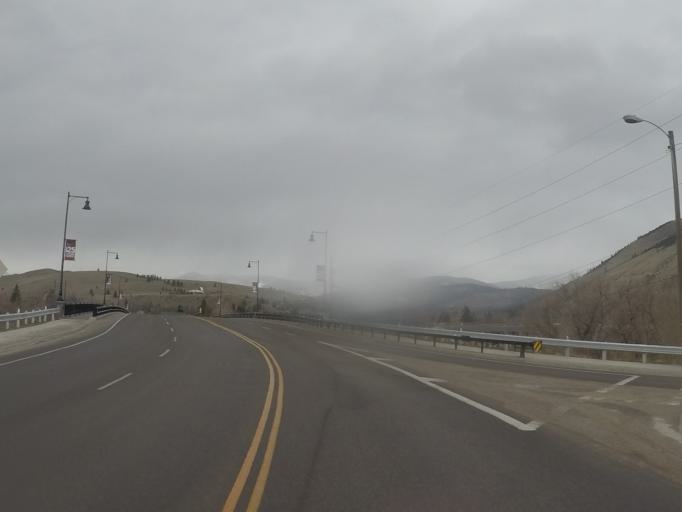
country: US
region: Montana
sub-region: Missoula County
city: Missoula
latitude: 46.8658
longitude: -113.9882
